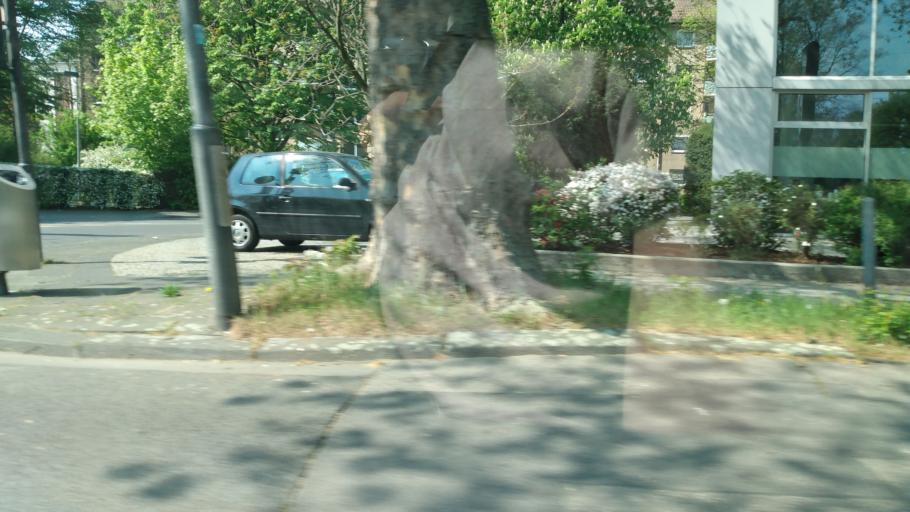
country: DE
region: North Rhine-Westphalia
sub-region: Regierungsbezirk Koln
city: Buchforst
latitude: 50.9573
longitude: 7.0008
